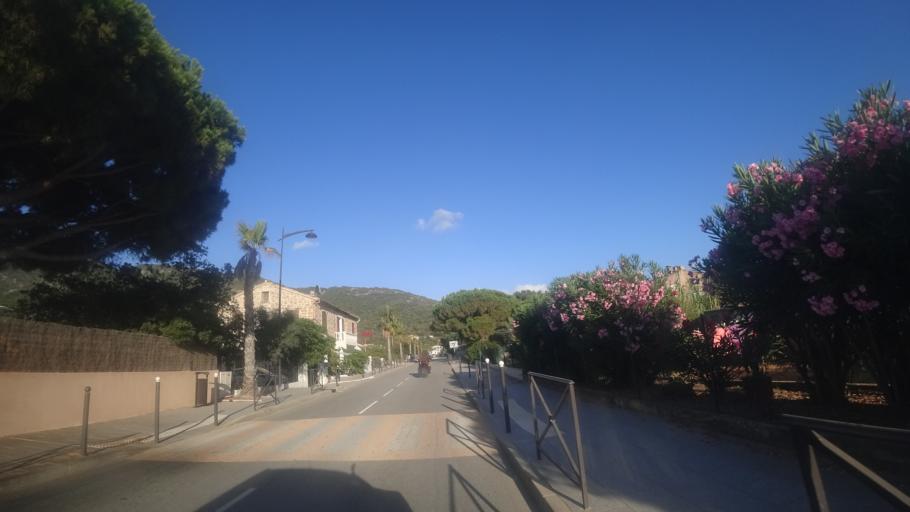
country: FR
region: Corsica
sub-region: Departement de la Corse-du-Sud
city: Cargese
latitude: 42.1144
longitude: 8.6977
